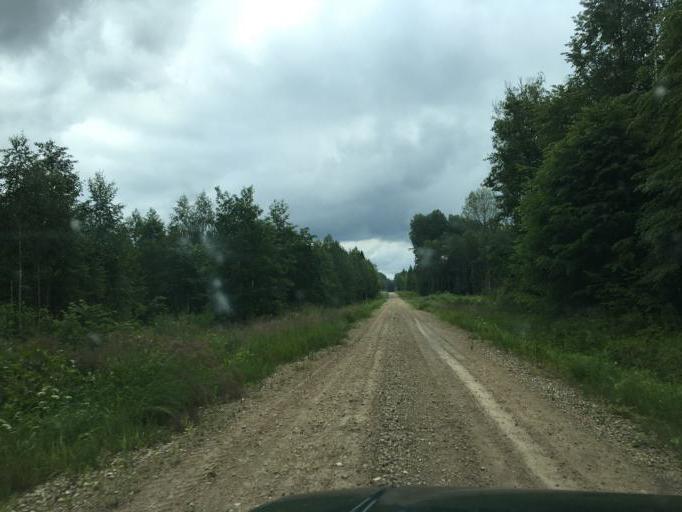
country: LV
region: Vilaka
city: Vilaka
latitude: 57.3820
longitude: 27.5272
